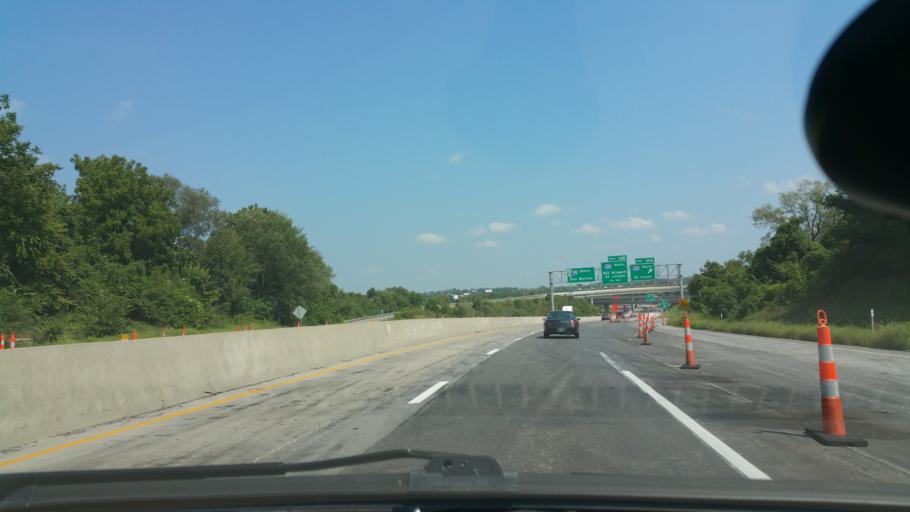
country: US
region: Missouri
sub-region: Clay County
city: Claycomo
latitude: 39.2047
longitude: -94.4983
